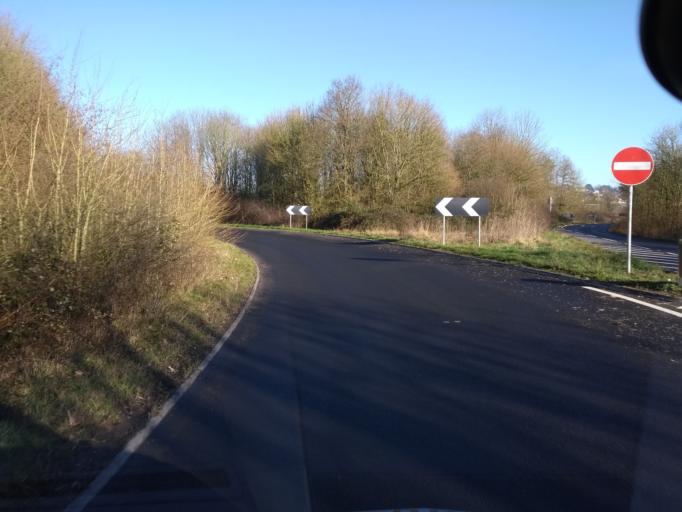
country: GB
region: England
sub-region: Somerset
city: Wincanton
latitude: 51.0472
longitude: -2.4154
